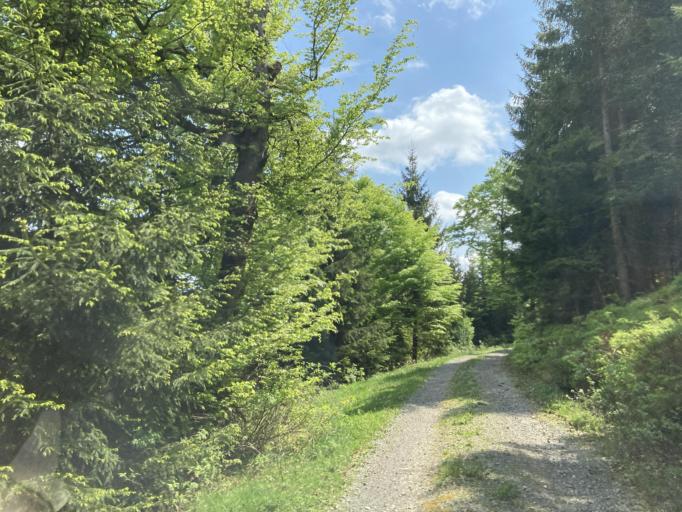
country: DE
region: Baden-Wuerttemberg
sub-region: Karlsruhe Region
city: Biberach
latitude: 48.5275
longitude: 8.2945
